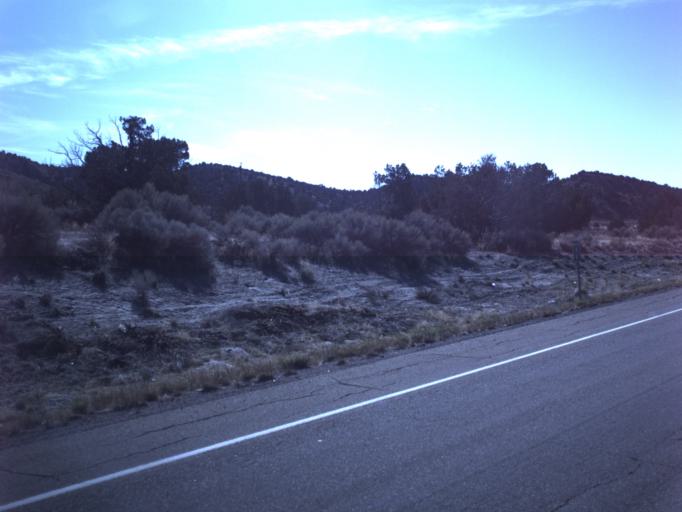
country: US
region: Utah
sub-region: Sanpete County
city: Gunnison
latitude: 39.3669
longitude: -111.9296
